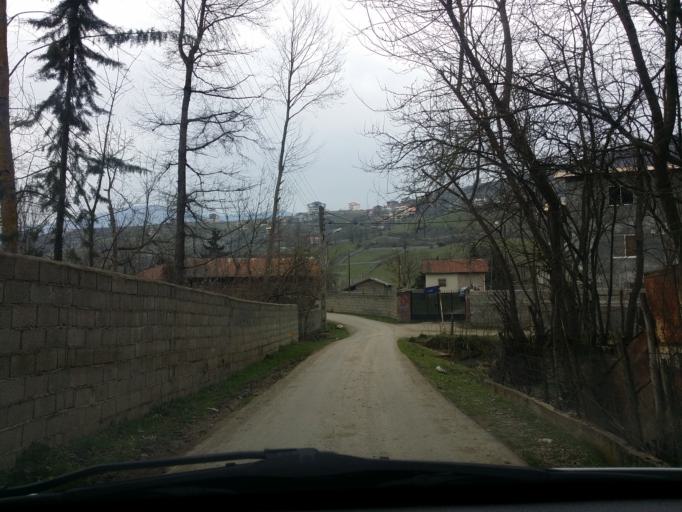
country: IR
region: Mazandaran
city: `Abbasabad
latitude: 36.5472
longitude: 51.1661
